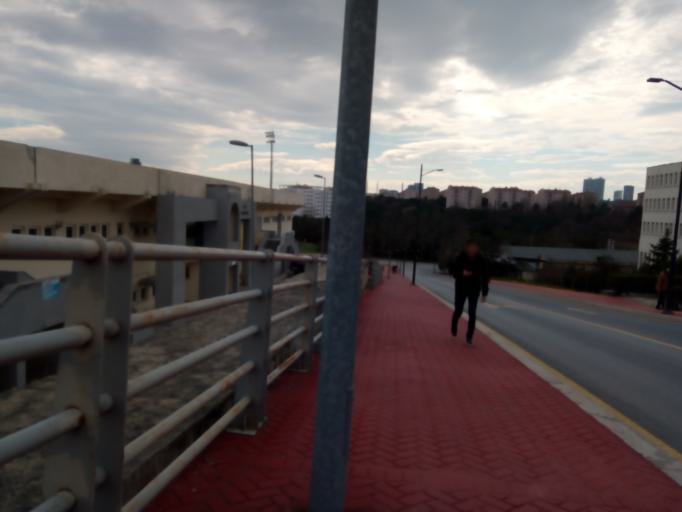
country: TR
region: Istanbul
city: Sisli
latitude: 41.1019
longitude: 29.0223
